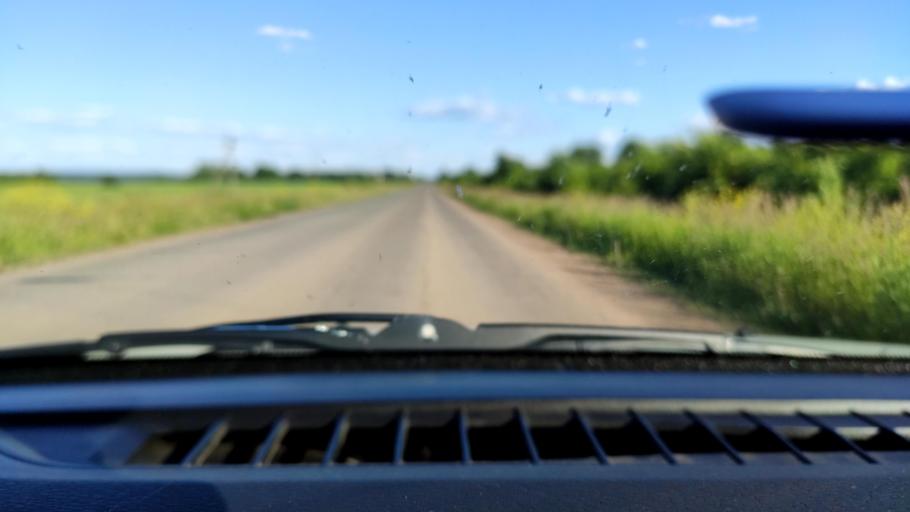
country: RU
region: Perm
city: Uinskoye
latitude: 57.1043
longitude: 56.5357
